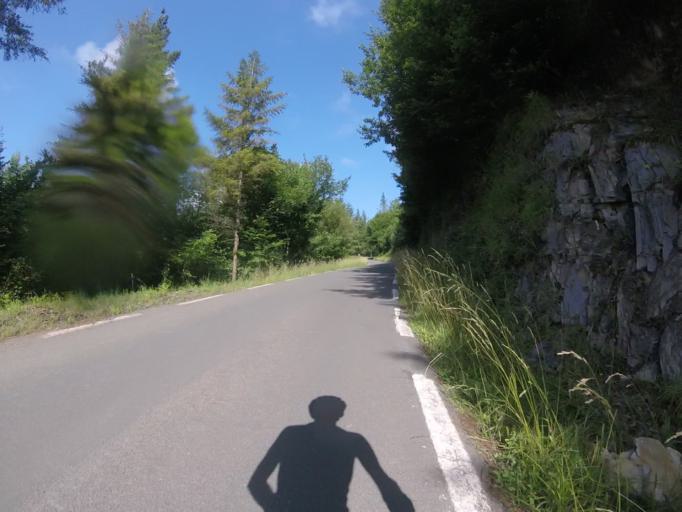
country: ES
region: Basque Country
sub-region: Provincia de Guipuzcoa
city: Beasain
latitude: 43.0811
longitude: -2.2223
